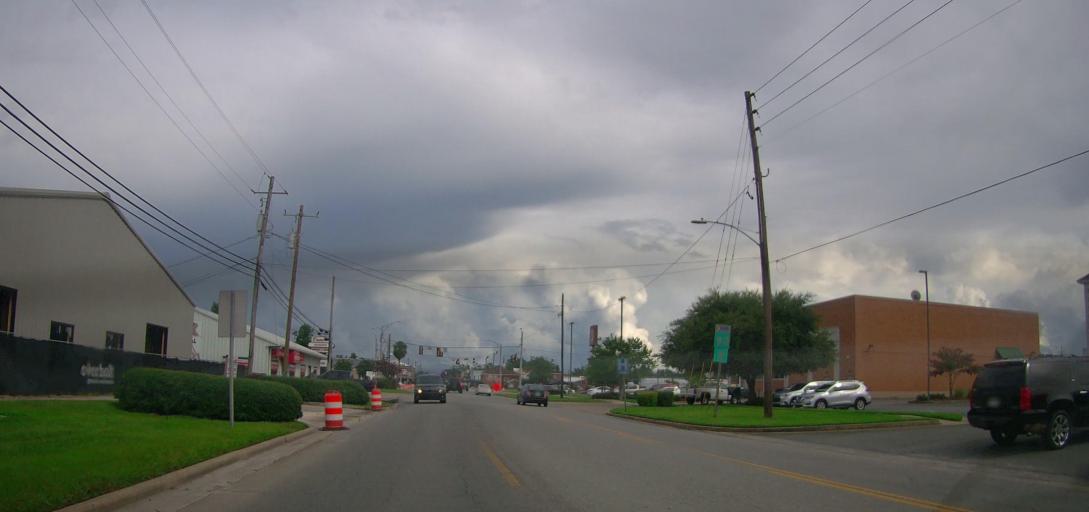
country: US
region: Georgia
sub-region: Wayne County
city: Jesup
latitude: 31.6080
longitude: -81.8863
